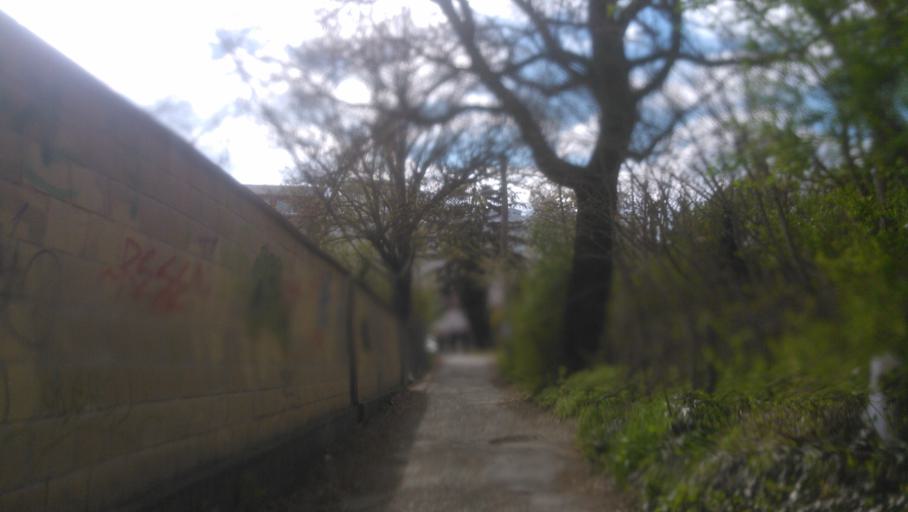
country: SK
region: Bratislavsky
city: Bratislava
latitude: 48.1553
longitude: 17.0717
